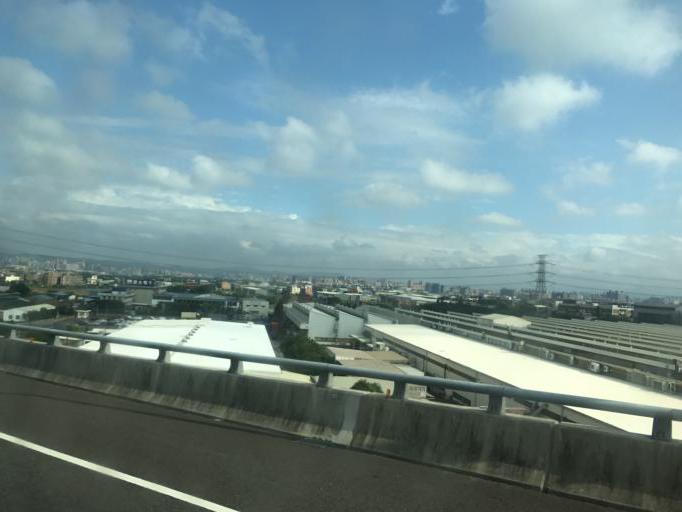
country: TW
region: Taiwan
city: Taoyuan City
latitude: 24.9964
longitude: 121.2457
